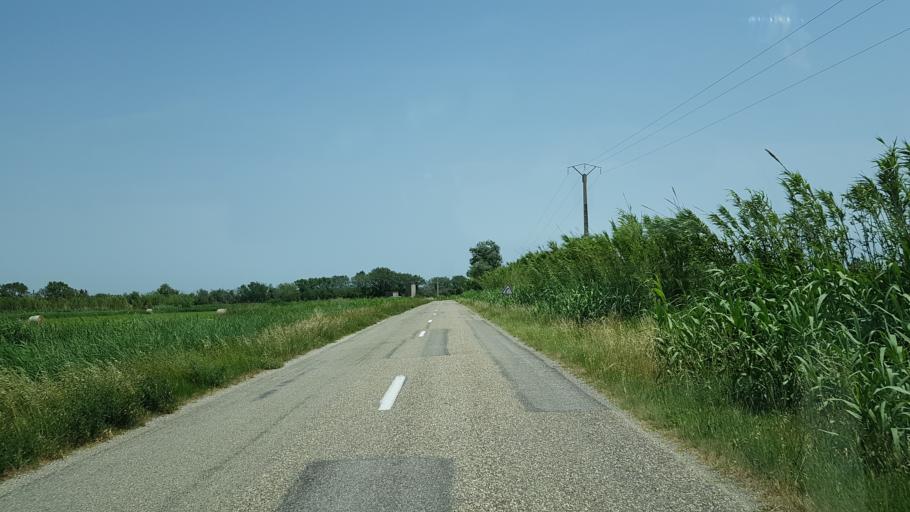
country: FR
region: Provence-Alpes-Cote d'Azur
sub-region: Departement des Bouches-du-Rhone
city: Port-Saint-Louis-du-Rhone
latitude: 43.4444
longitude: 4.6714
